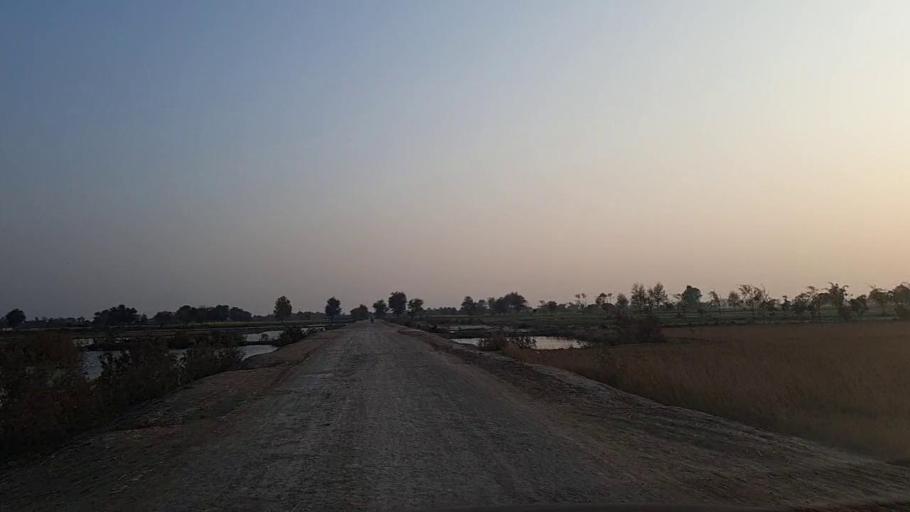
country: PK
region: Sindh
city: Daur
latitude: 26.4214
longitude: 68.3678
